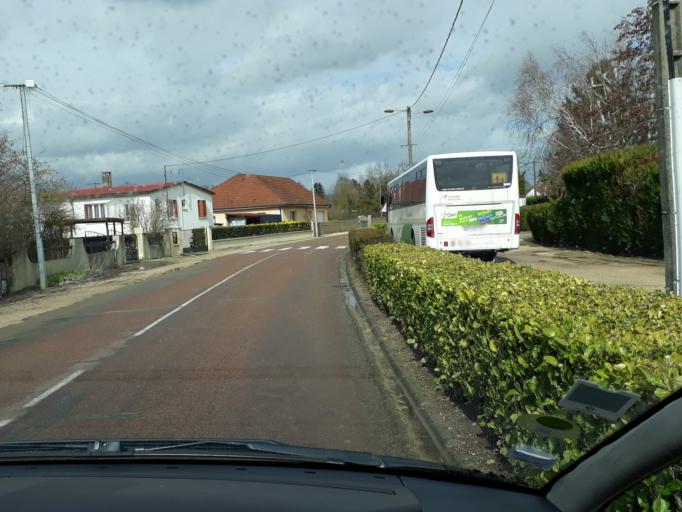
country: FR
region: Bourgogne
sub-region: Departement de la Cote-d'Or
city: Longecourt-en-Plaine
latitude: 47.2110
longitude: 5.1826
